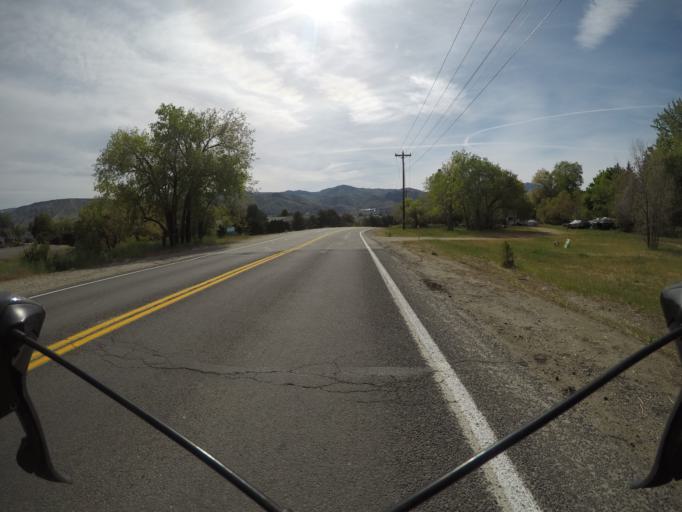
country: US
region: Washington
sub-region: Douglas County
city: East Wenatchee Bench
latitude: 47.4129
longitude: -120.2780
